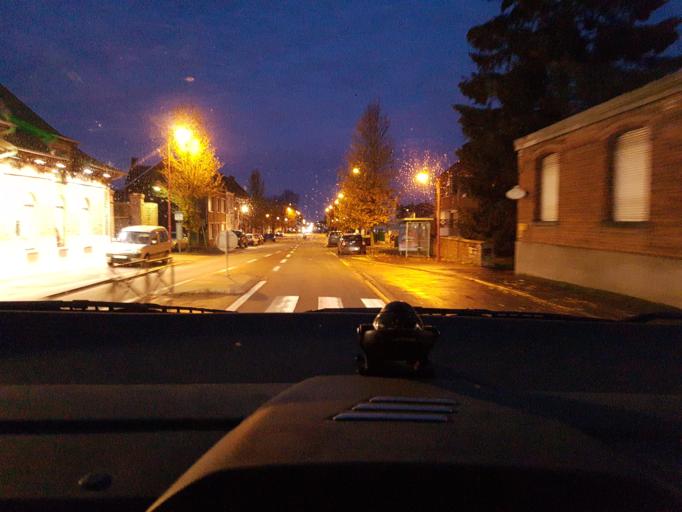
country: FR
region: Nord-Pas-de-Calais
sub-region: Departement du Pas-de-Calais
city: Beaumetz-les-Loges
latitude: 50.2417
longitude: 2.6600
